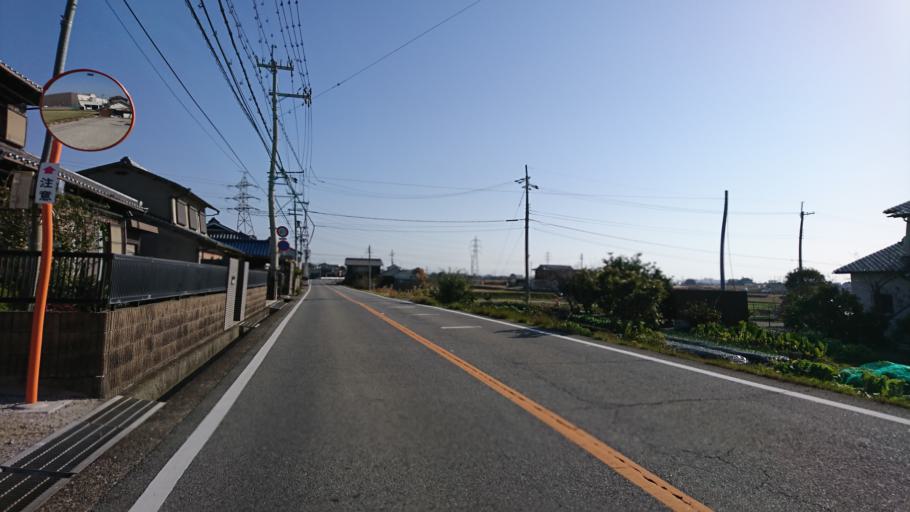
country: JP
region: Hyogo
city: Kakogawacho-honmachi
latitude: 34.7625
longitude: 134.8938
